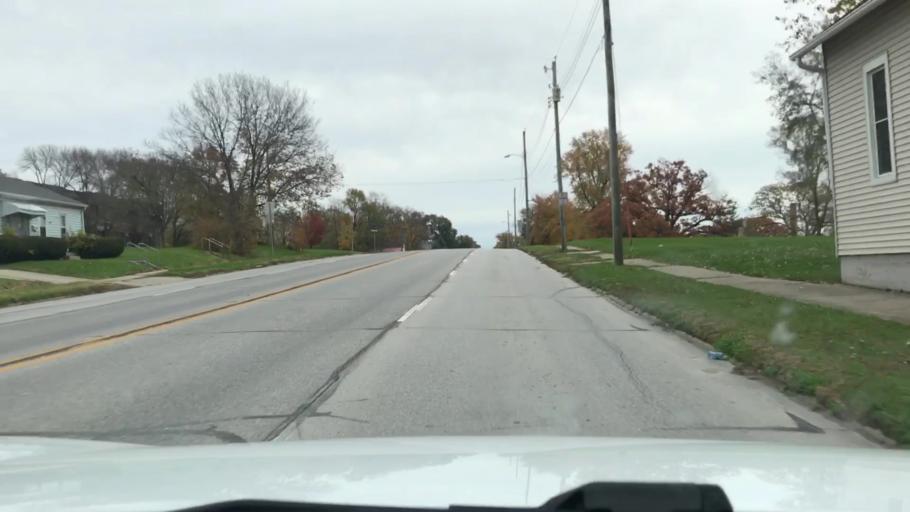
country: US
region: Iowa
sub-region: Lee County
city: Keokuk
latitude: 40.3908
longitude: -91.4024
